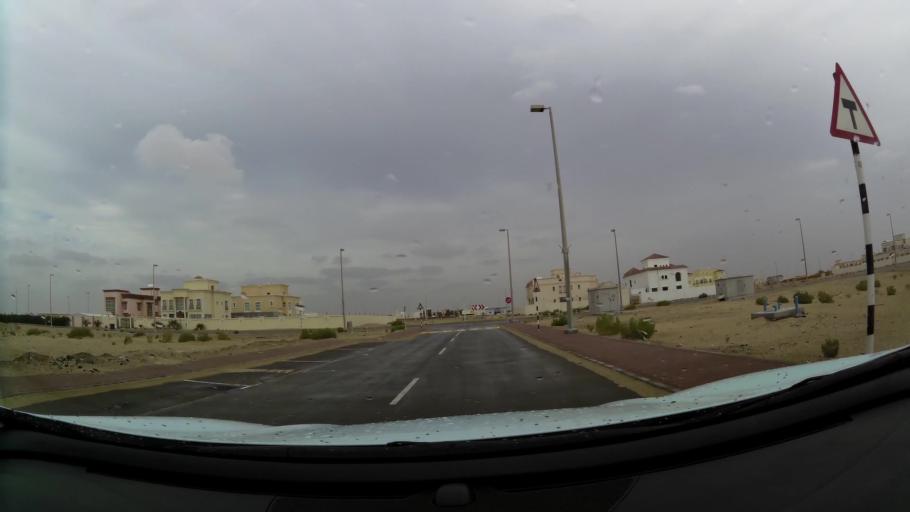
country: AE
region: Abu Dhabi
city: Abu Dhabi
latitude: 24.3658
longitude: 54.6226
